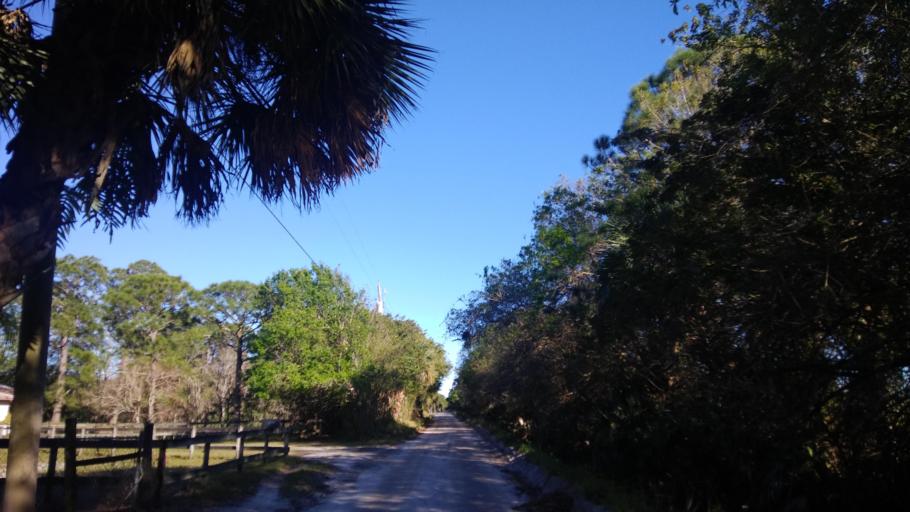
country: US
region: Florida
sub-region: Indian River County
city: Fellsmere
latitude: 27.7537
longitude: -80.5830
